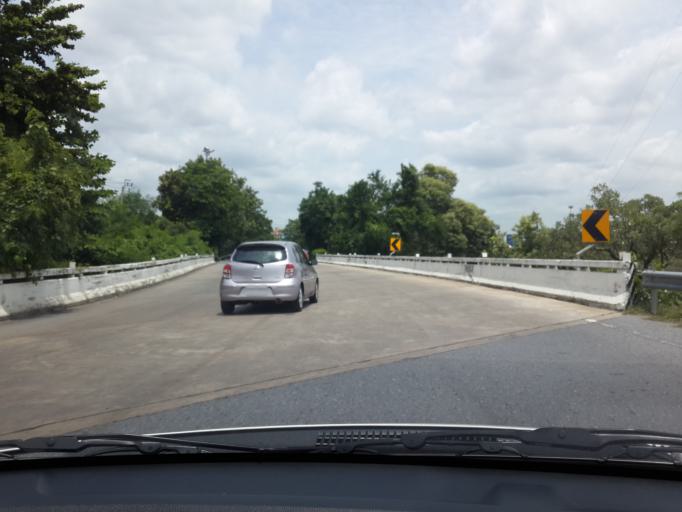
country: TH
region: Bangkok
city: Saphan Sung
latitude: 13.7799
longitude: 100.6853
